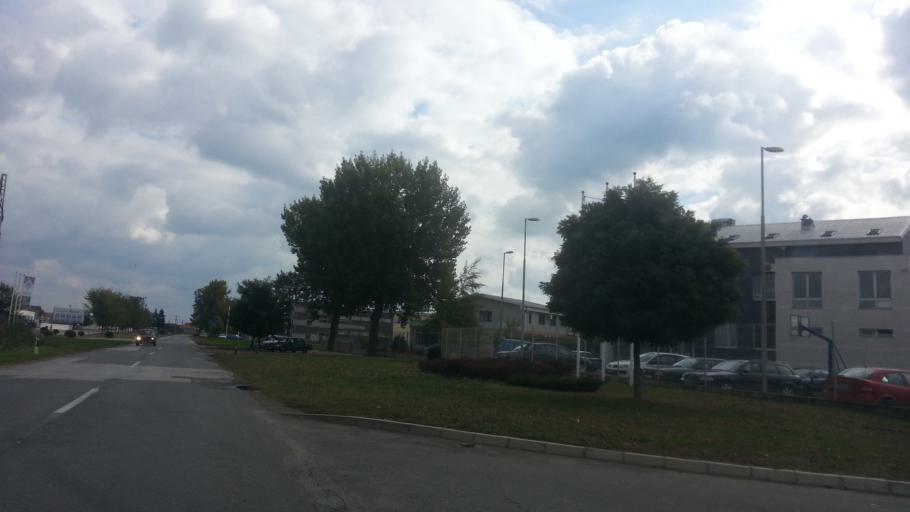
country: RS
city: Stari Banovci
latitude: 44.9863
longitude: 20.2591
